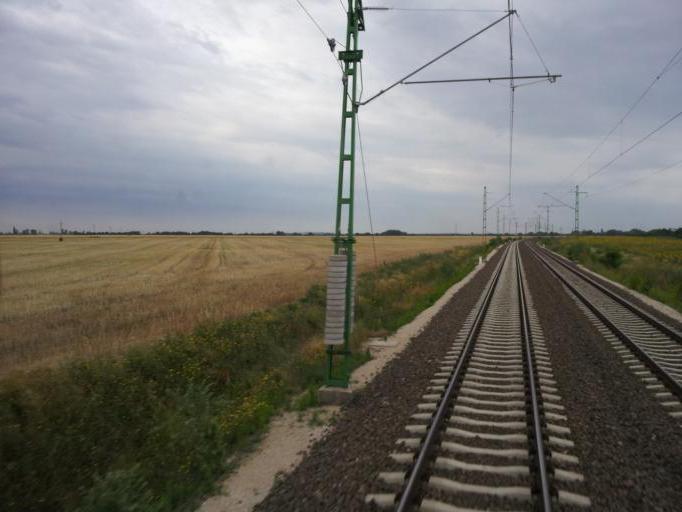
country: HU
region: Fejer
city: Pakozd
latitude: 47.1710
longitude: 18.4834
